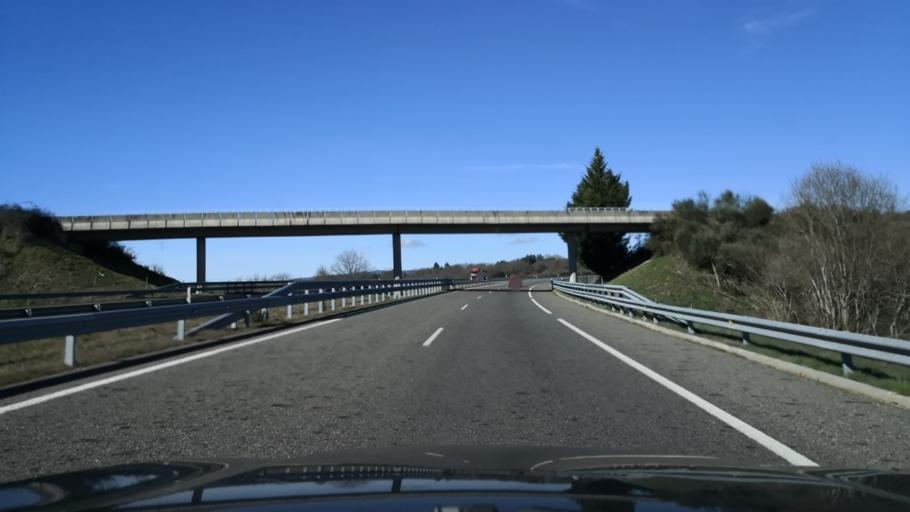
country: ES
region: Galicia
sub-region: Provincia de Ourense
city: Trasmiras
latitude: 42.0327
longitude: -7.6547
